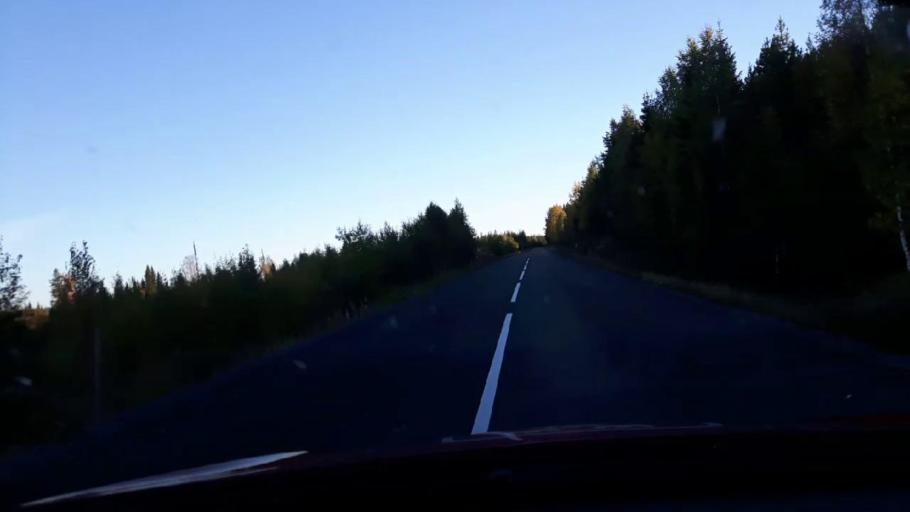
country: SE
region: Jaemtland
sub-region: OEstersunds Kommun
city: Lit
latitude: 63.4775
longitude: 14.8800
